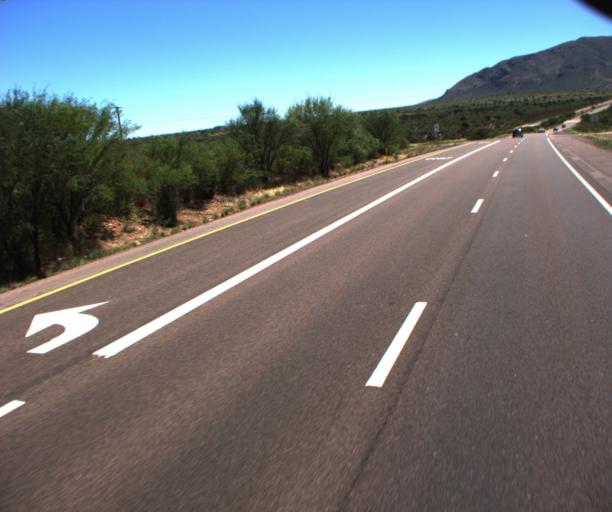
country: US
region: Arizona
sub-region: Gila County
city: Payson
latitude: 34.0632
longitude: -111.3610
